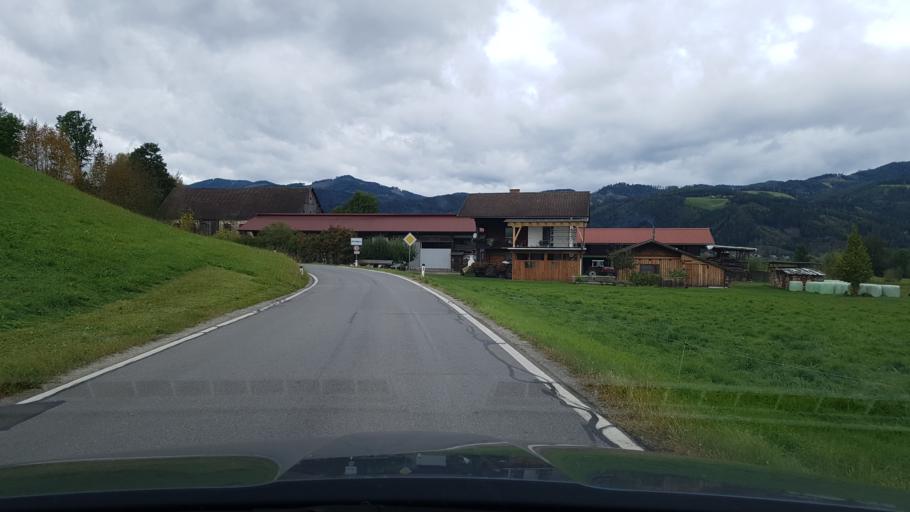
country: AT
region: Styria
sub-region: Politischer Bezirk Bruck-Muerzzuschlag
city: Allerheiligen im Muerztal
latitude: 47.4748
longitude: 15.4134
